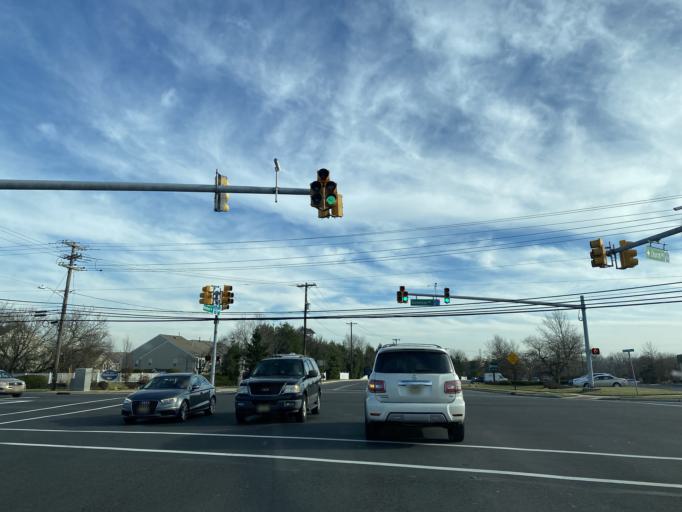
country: US
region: New Jersey
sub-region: Burlington County
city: Marlton
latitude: 39.9152
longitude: -74.9215
